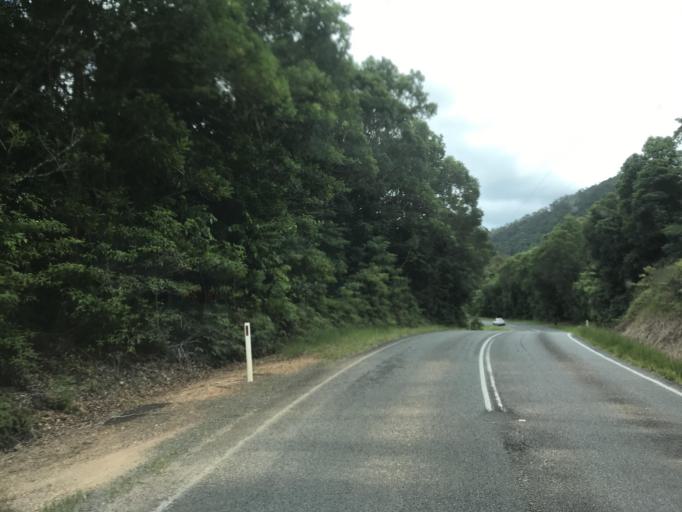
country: AU
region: Queensland
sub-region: Cassowary Coast
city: Innisfail
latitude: -17.8306
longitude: 146.0543
